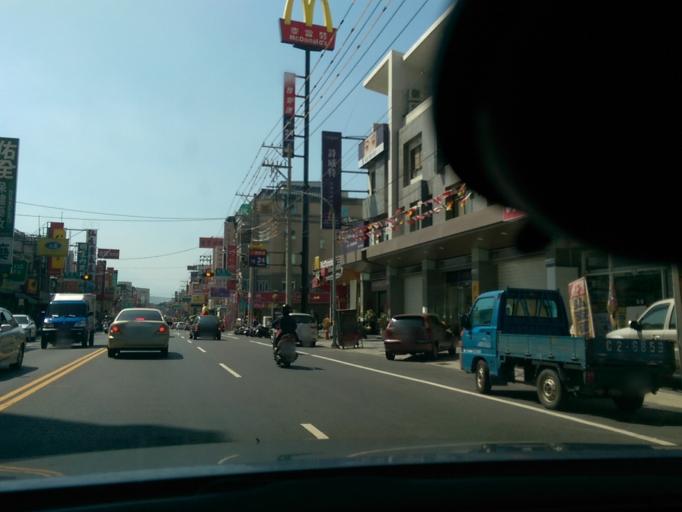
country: TW
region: Taiwan
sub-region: Chiayi
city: Jiayi Shi
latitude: 23.4571
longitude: 120.4585
